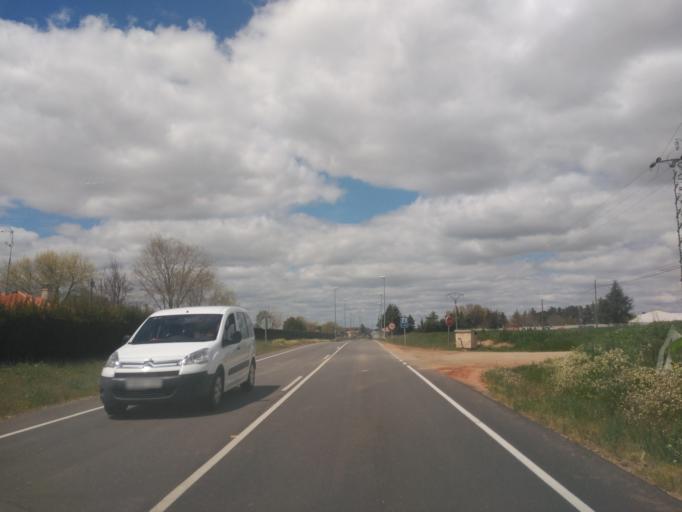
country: ES
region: Castille and Leon
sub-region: Provincia de Salamanca
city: Villamayor
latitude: 41.0071
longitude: -5.7049
